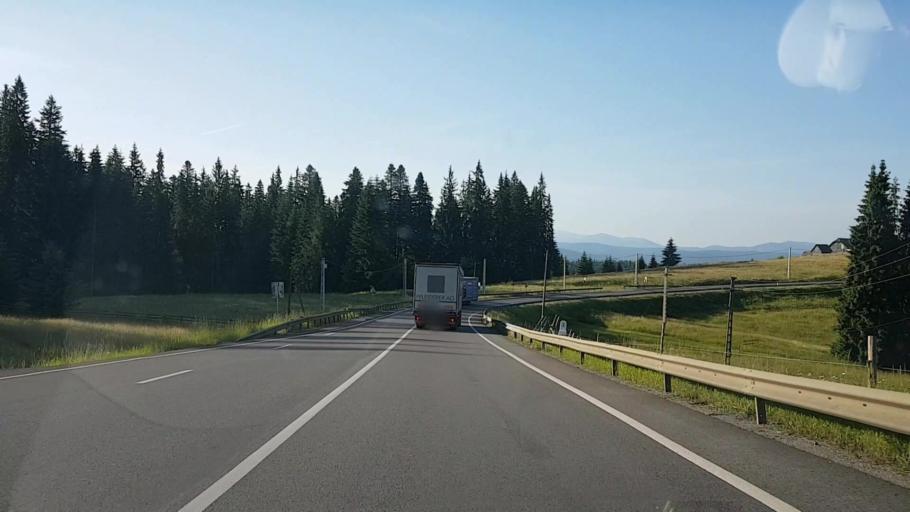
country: RO
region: Suceava
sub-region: Comuna Poiana Stampei
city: Poiana Stampei
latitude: 47.2902
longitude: 25.0770
